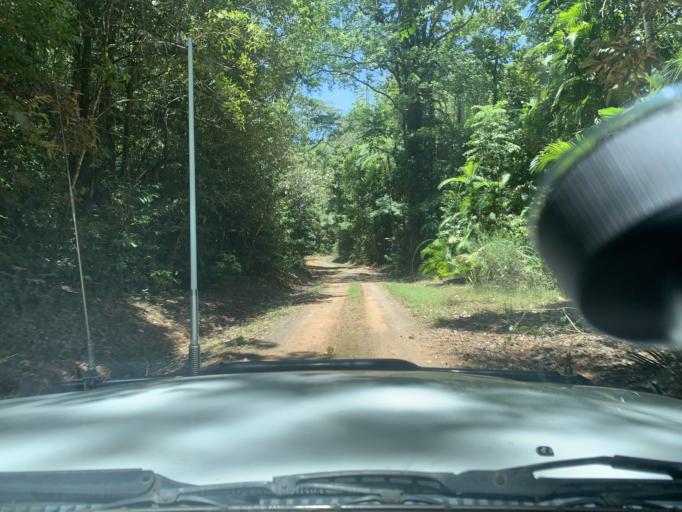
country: AU
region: Queensland
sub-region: Cairns
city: Redlynch
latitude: -16.9700
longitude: 145.6494
